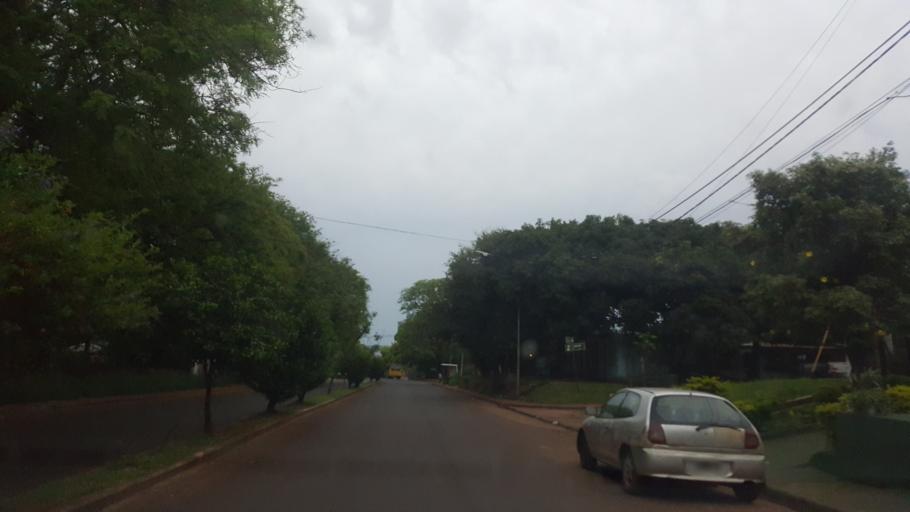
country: AR
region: Misiones
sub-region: Departamento de Capital
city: Posadas
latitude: -27.3576
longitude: -55.9380
